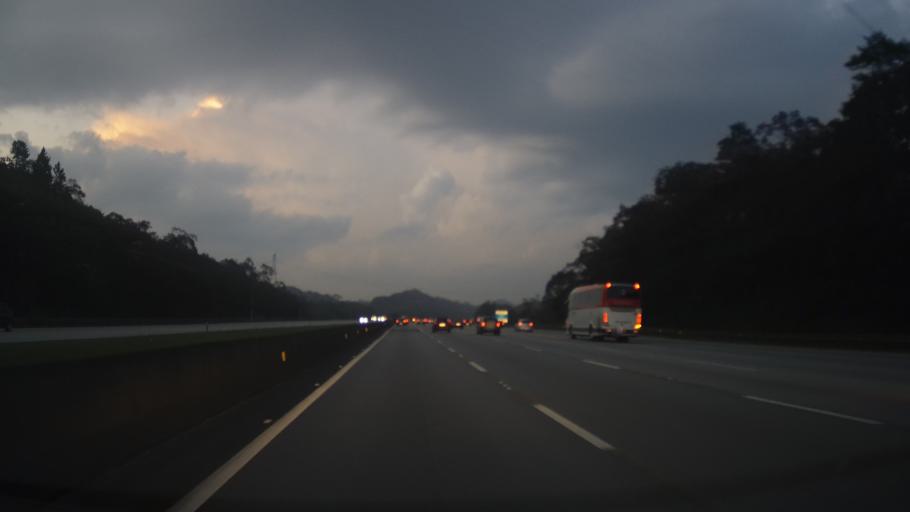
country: BR
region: Sao Paulo
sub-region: Cubatao
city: Cubatao
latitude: -23.8698
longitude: -46.5718
